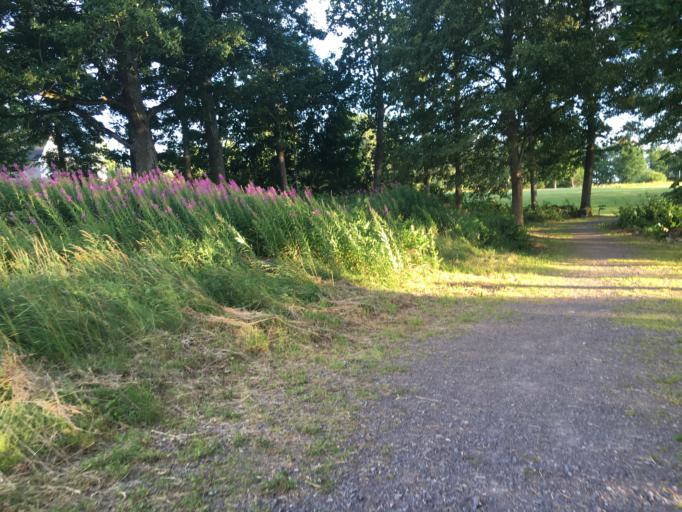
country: SE
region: Kalmar
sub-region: Nybro Kommun
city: Nybro
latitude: 56.9421
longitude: 15.9104
